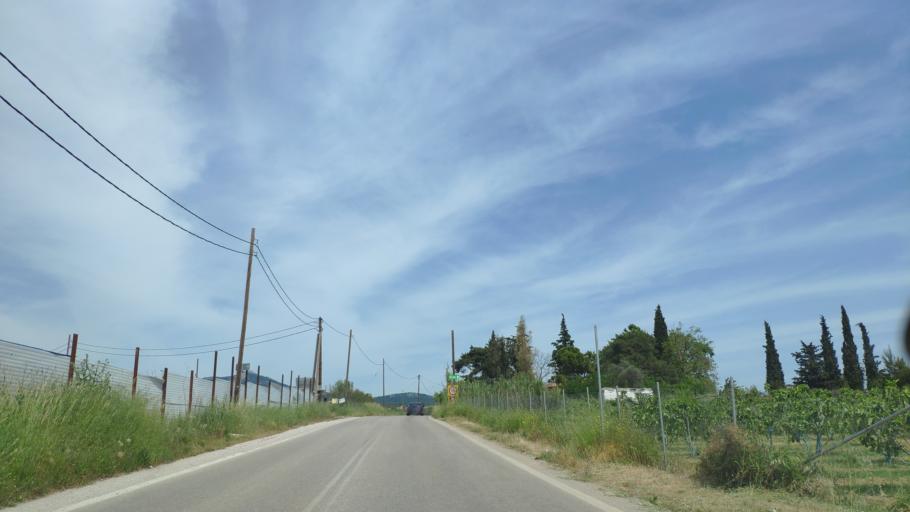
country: GR
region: Attica
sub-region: Nomarchia Anatolikis Attikis
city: Afidnes
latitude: 38.1784
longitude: 23.8581
